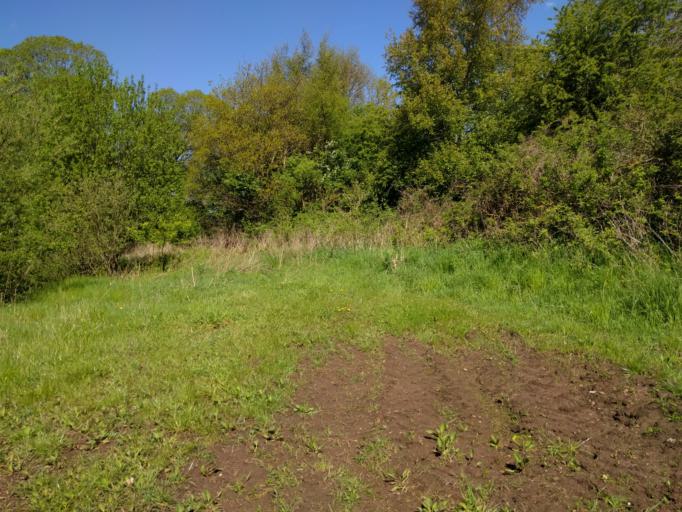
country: DK
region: South Denmark
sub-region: Kerteminde Kommune
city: Langeskov
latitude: 55.3852
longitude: 10.5514
